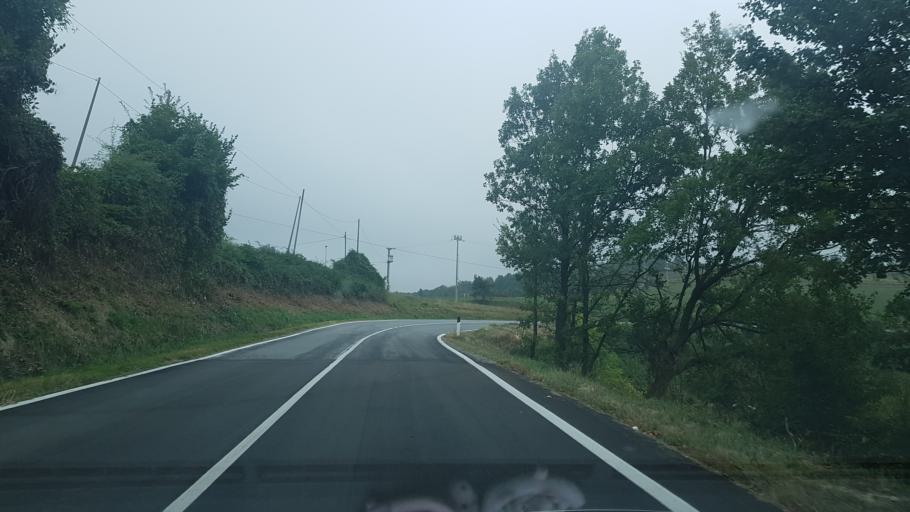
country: IT
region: Piedmont
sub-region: Provincia di Cuneo
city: Paroldo
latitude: 44.4202
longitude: 8.0920
